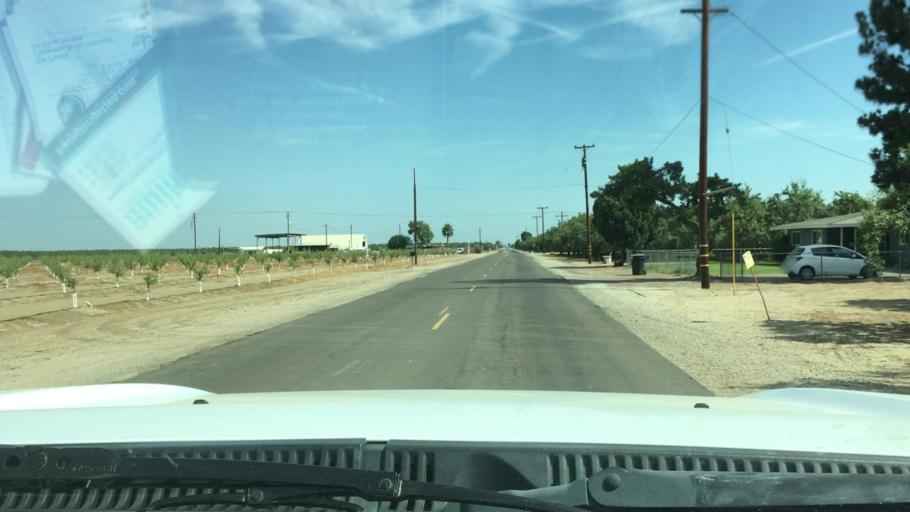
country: US
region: California
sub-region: Kern County
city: Shafter
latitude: 35.5126
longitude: -119.3499
